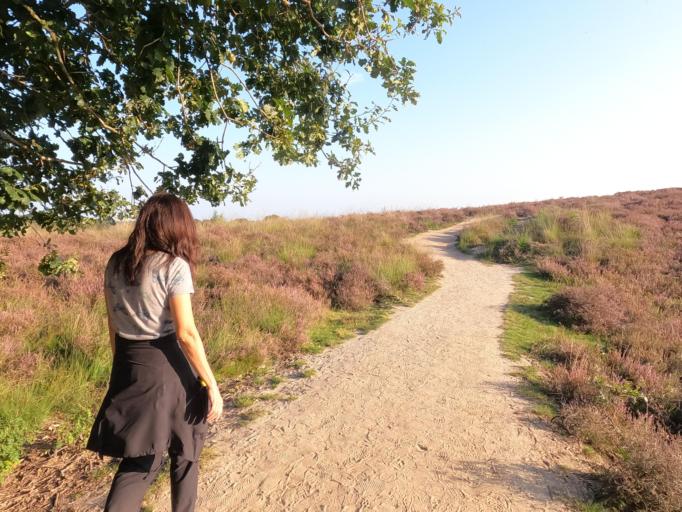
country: NL
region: Gelderland
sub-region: Gemeente Rheden
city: Rheden
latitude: 52.0255
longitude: 6.0269
